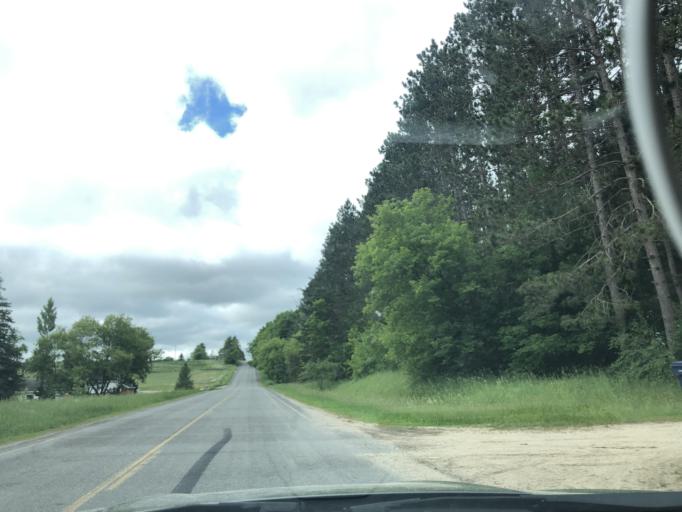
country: US
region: Michigan
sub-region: Missaukee County
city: Lake City
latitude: 44.4532
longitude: -85.2160
